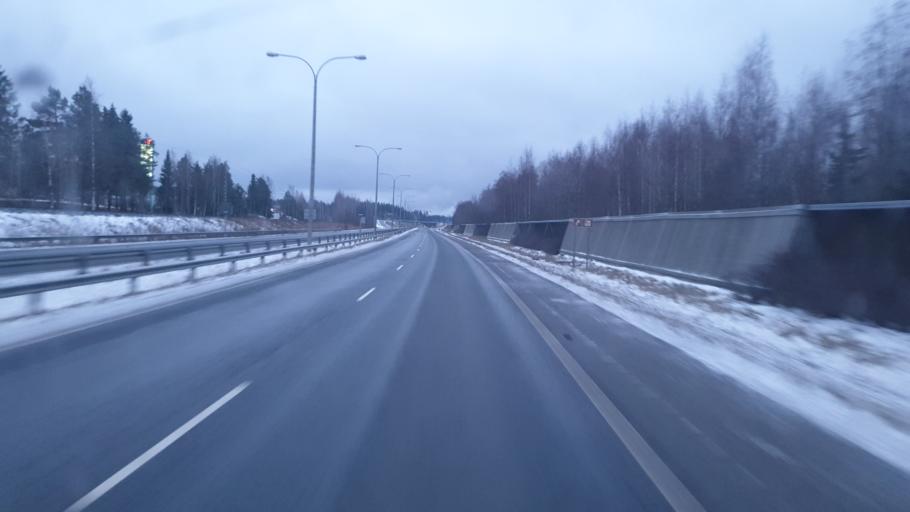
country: FI
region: Northern Savo
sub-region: Kuopio
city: Kuopio
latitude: 62.9804
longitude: 27.7058
